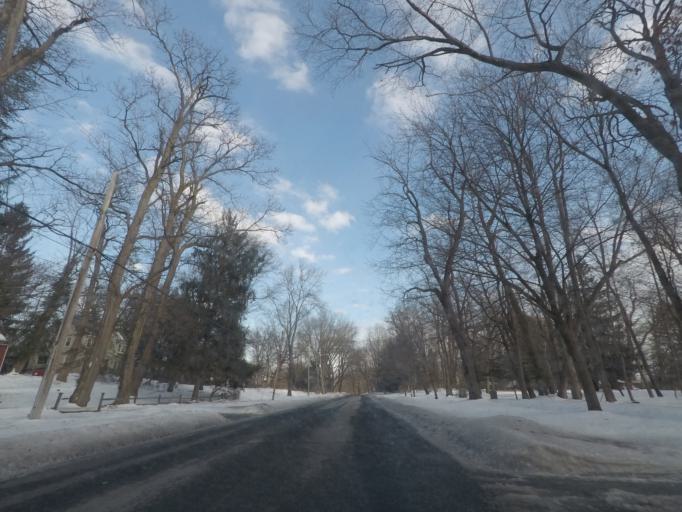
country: US
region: New York
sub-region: Schenectady County
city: Scotia
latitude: 42.8297
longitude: -73.9531
